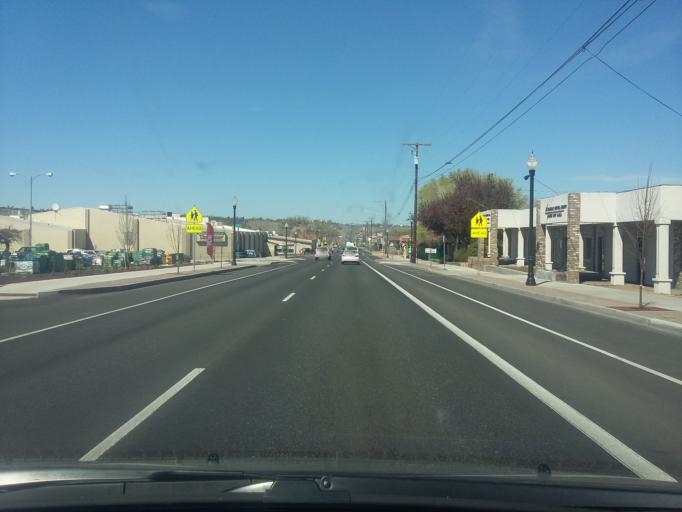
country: US
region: Oregon
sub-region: Jefferson County
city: Madras
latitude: 44.6269
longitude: -121.1296
